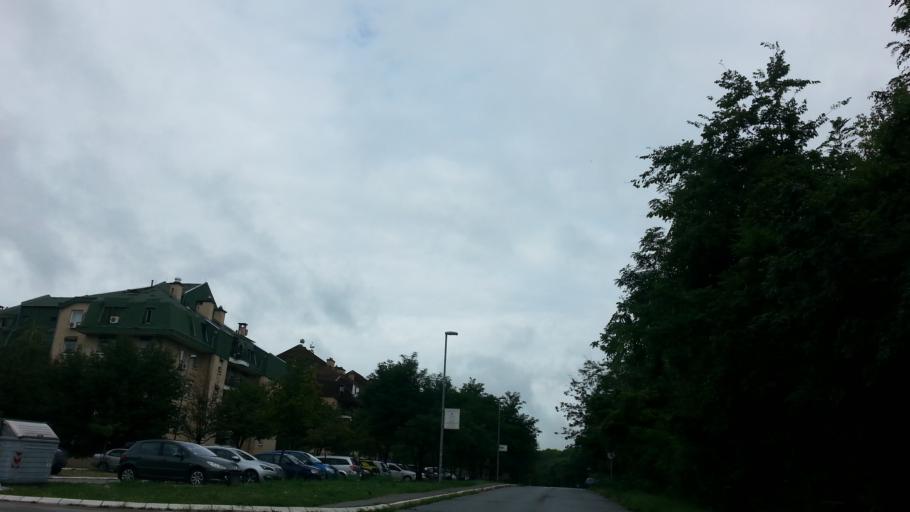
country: RS
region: Central Serbia
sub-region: Belgrade
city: Rakovica
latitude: 44.7537
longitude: 20.4300
